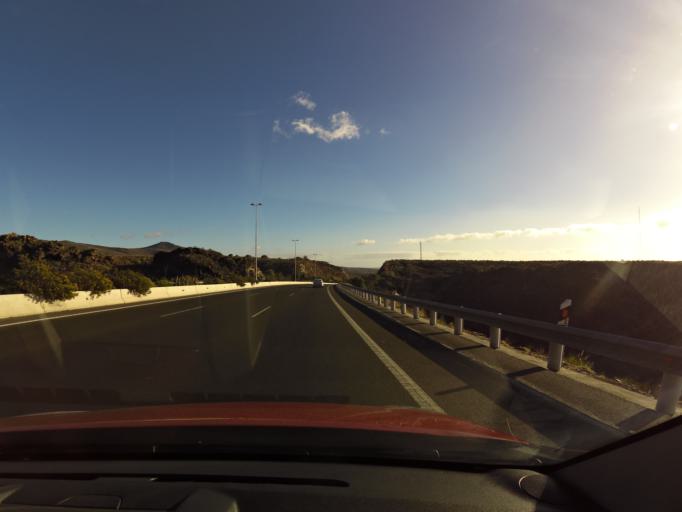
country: ES
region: Canary Islands
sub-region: Provincia de Las Palmas
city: Playa del Ingles
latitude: 27.7795
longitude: -15.5419
